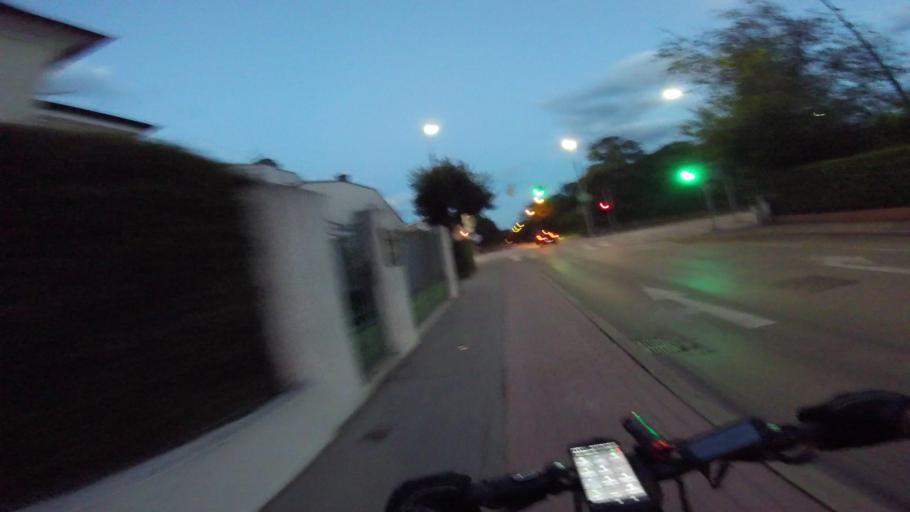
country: AT
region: Lower Austria
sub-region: Politischer Bezirk Modling
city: Modling
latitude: 48.0829
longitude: 16.2939
